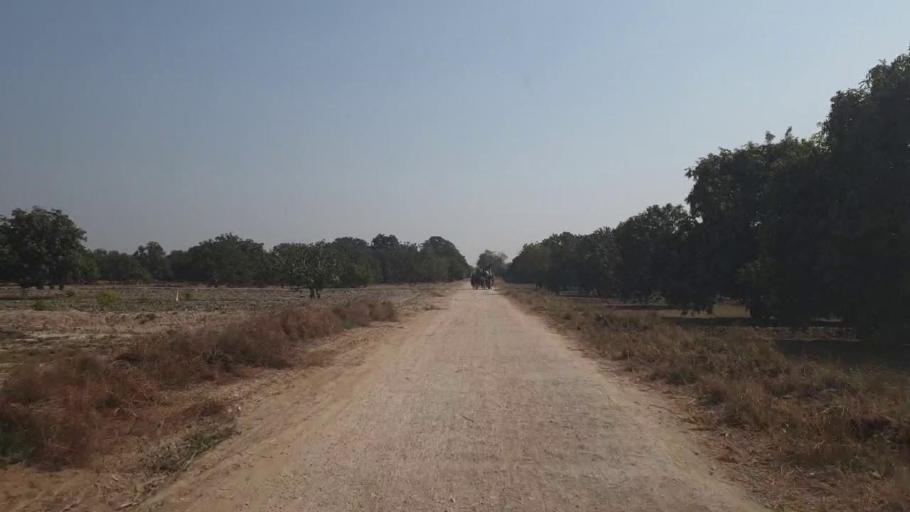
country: PK
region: Sindh
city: Tando Allahyar
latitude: 25.4511
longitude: 68.8284
